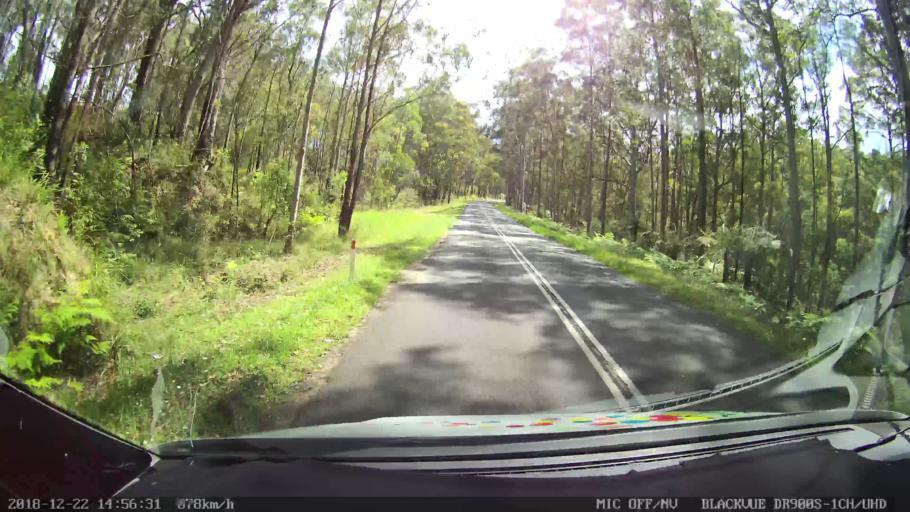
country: AU
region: New South Wales
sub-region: Bellingen
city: Dorrigo
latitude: -30.2331
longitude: 152.5114
